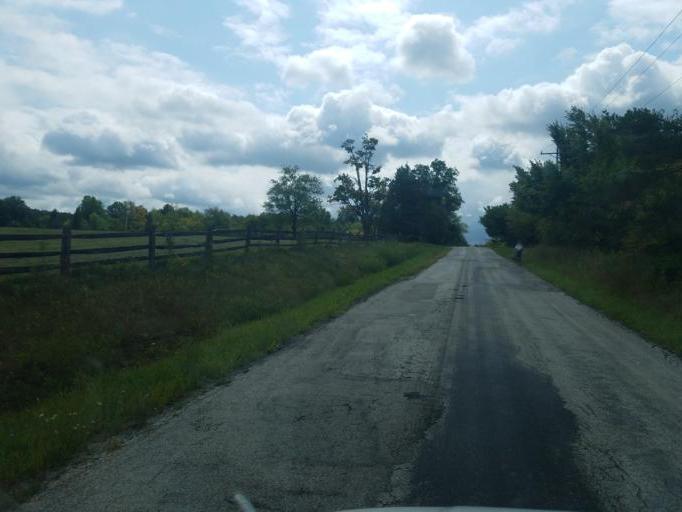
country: US
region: Ohio
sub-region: Geauga County
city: Chardon
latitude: 41.6466
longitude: -81.1127
